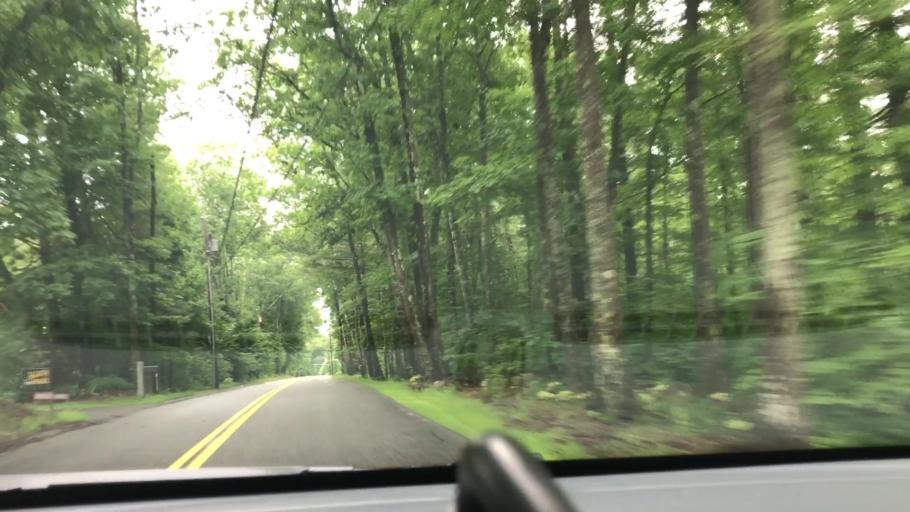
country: US
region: New Hampshire
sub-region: Hillsborough County
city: Pinardville
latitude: 42.9748
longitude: -71.5342
